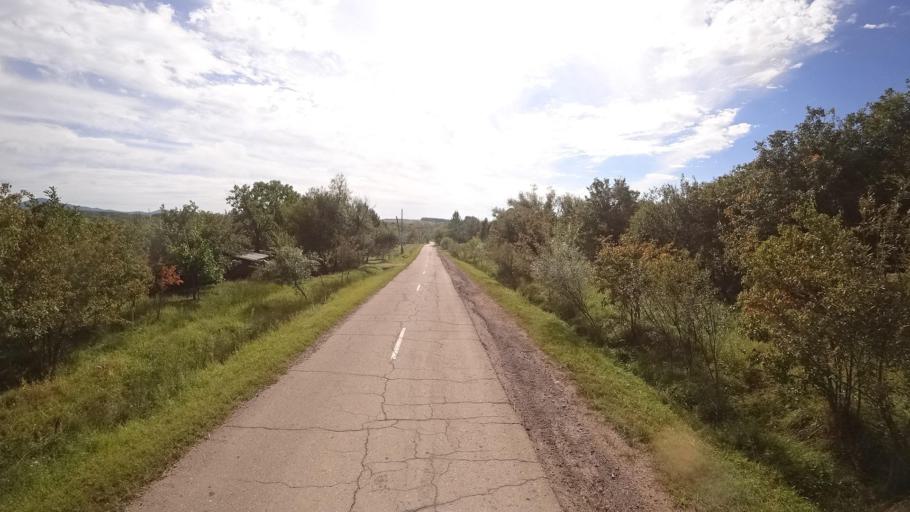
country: RU
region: Primorskiy
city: Dostoyevka
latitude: 44.3358
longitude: 133.4857
